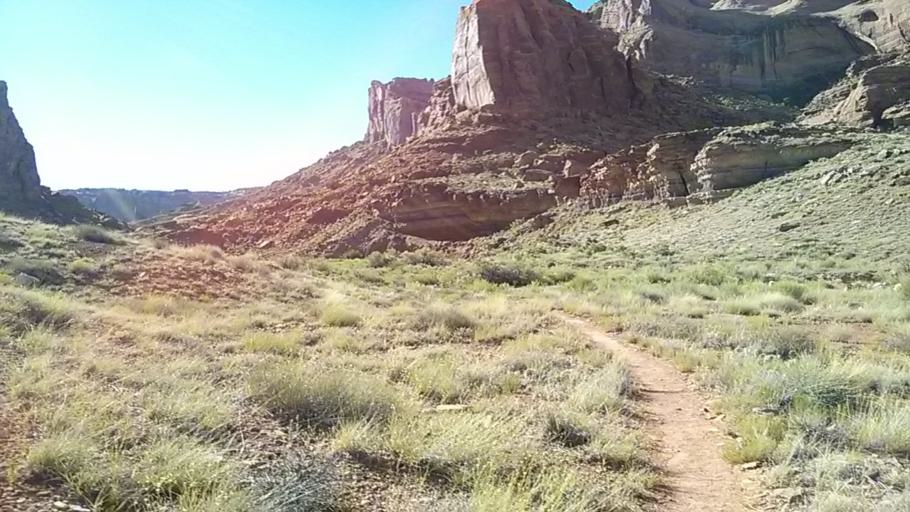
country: US
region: Utah
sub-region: Grand County
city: Moab
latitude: 38.4441
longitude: -109.9519
